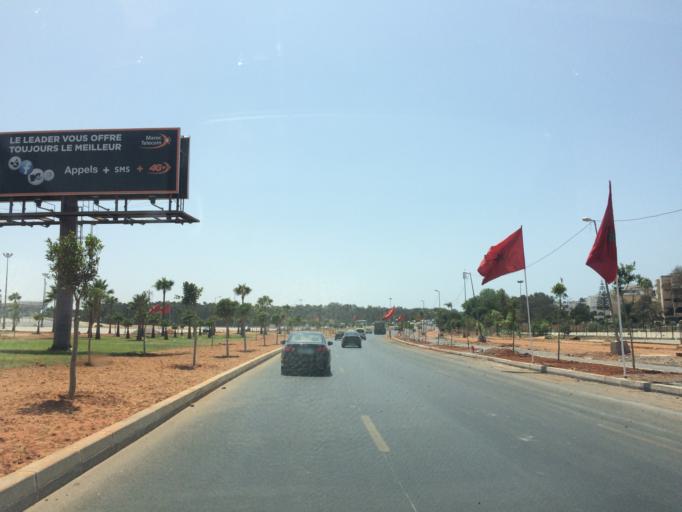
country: MA
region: Rabat-Sale-Zemmour-Zaer
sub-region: Skhirate-Temara
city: Temara
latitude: 33.9683
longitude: -6.8845
